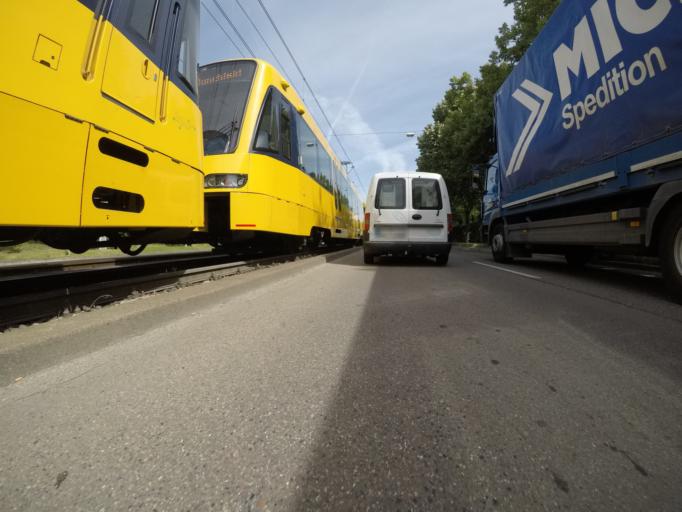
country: DE
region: Baden-Wuerttemberg
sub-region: Regierungsbezirk Stuttgart
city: Stuttgart
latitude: 48.7959
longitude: 9.1824
